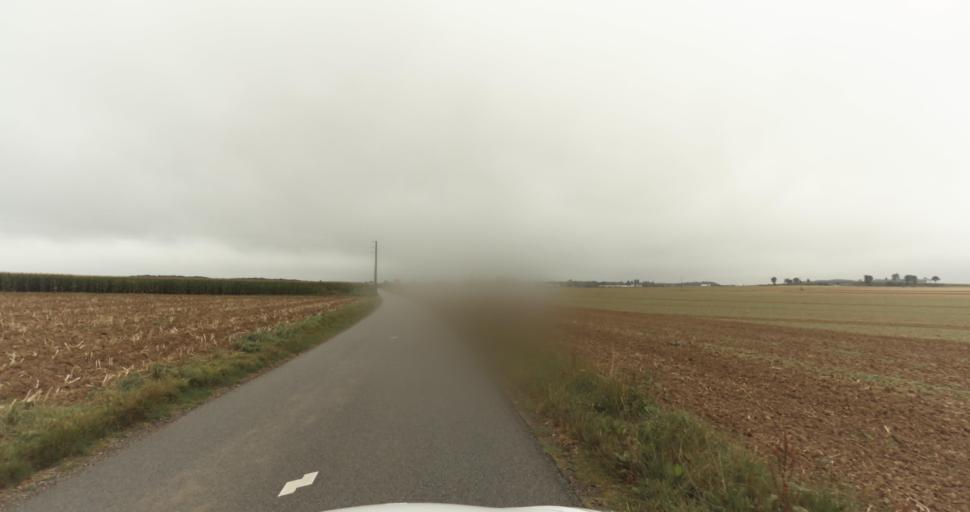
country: FR
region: Haute-Normandie
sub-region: Departement de l'Eure
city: Normanville
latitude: 49.0807
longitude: 1.1966
